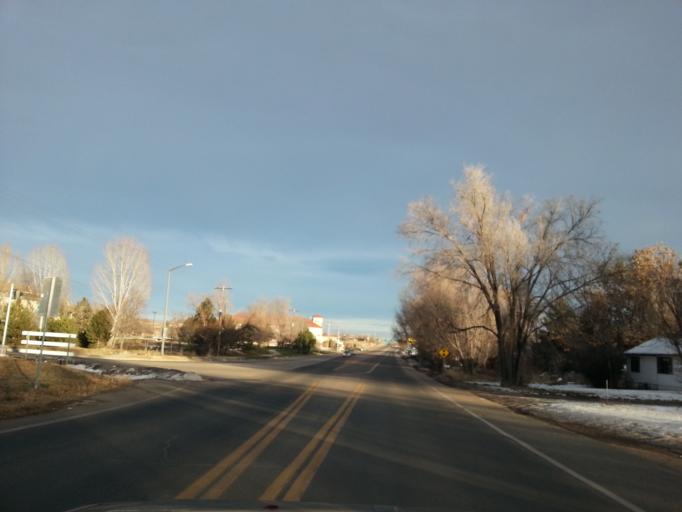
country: US
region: Colorado
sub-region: Larimer County
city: Loveland
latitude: 40.4073
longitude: -105.1347
